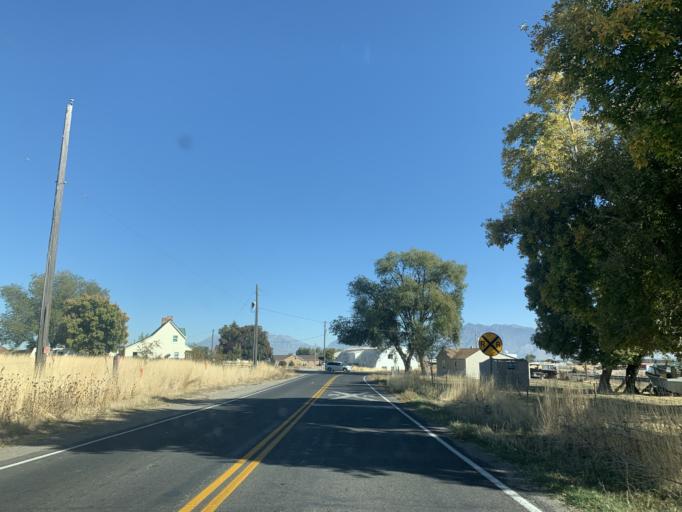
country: US
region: Utah
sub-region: Utah County
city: Payson
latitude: 40.0429
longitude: -111.7602
